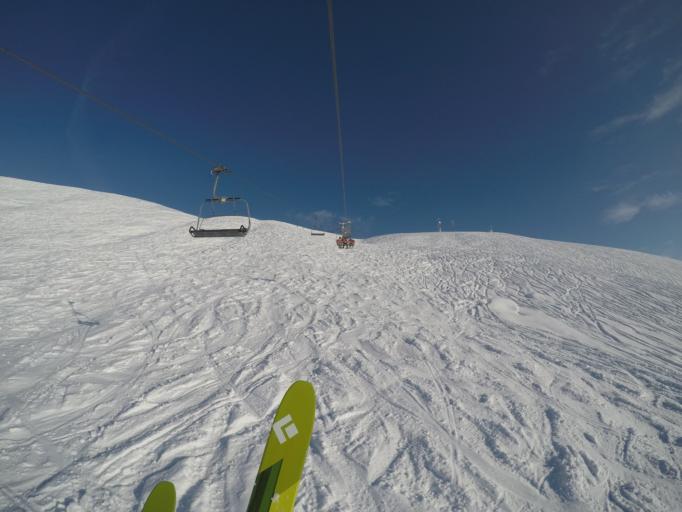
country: GE
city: Gudauri
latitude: 42.4856
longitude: 44.4965
